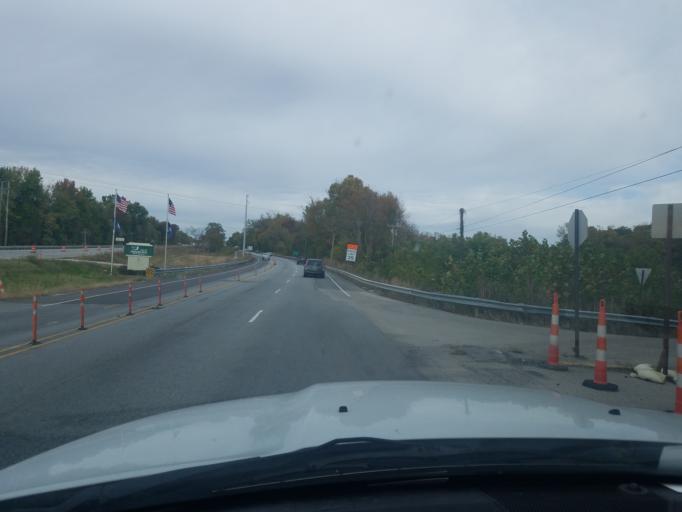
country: US
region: Kentucky
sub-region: Henderson County
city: Henderson
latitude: 37.8891
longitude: -87.5569
